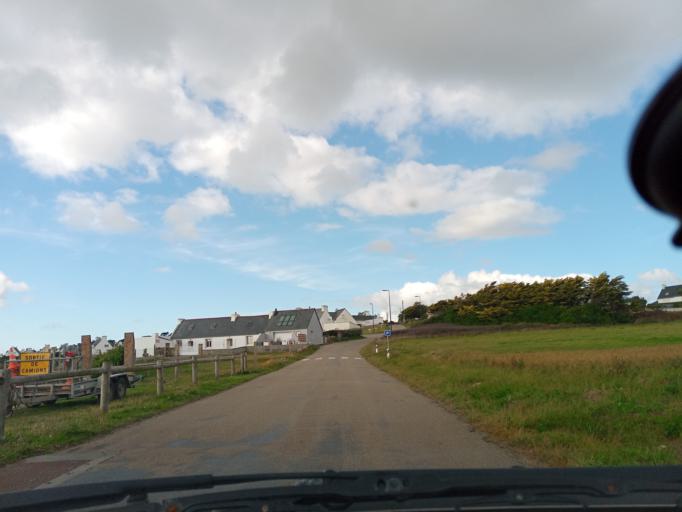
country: FR
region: Brittany
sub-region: Departement du Finistere
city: Plozevet
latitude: 47.9801
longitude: -4.4492
